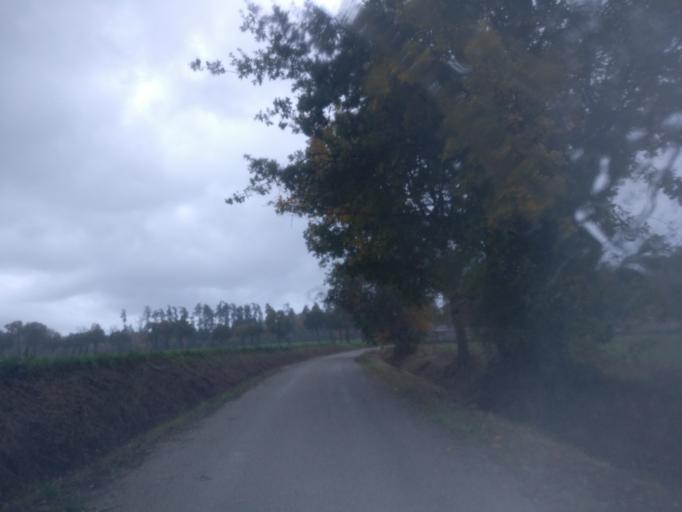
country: FR
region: Brittany
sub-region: Departement d'Ille-et-Vilaine
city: Bruz
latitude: 48.0198
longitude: -1.7718
